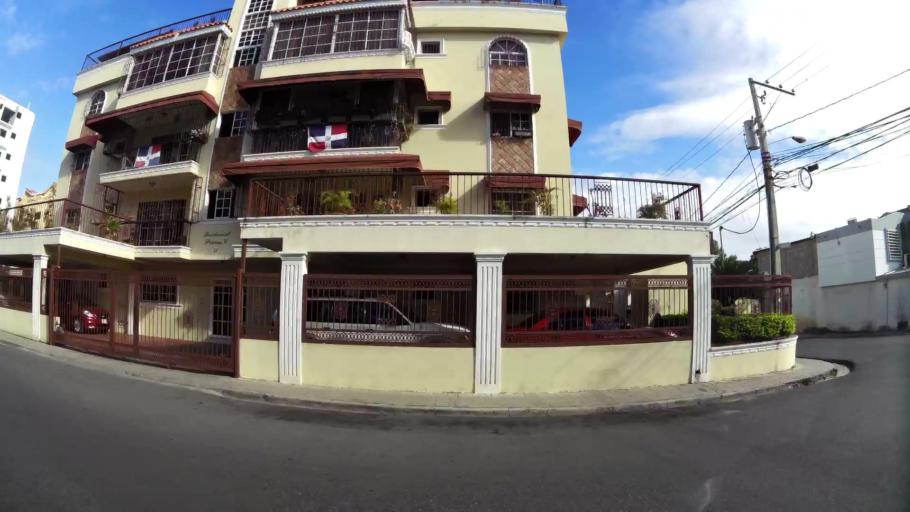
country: DO
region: Nacional
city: La Julia
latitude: 18.4741
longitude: -69.9472
